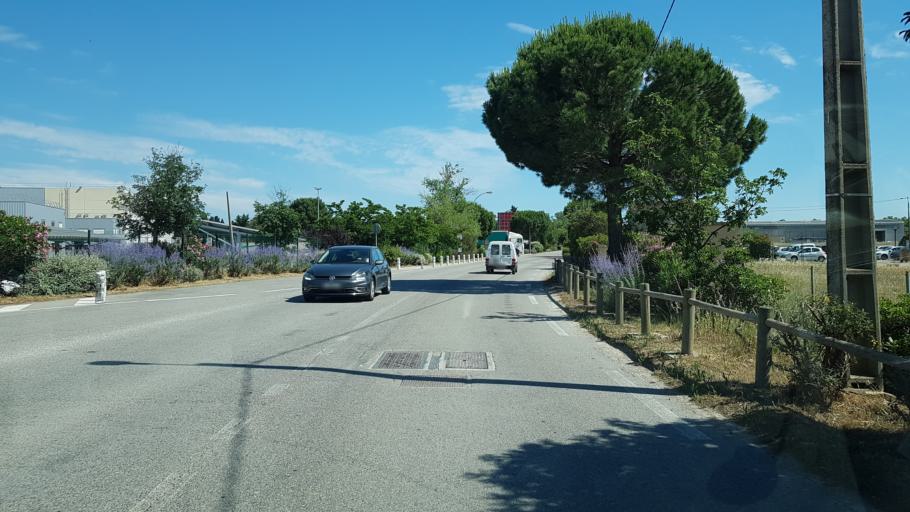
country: FR
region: Provence-Alpes-Cote d'Azur
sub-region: Departement des Bouches-du-Rhone
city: Saint-Martin-de-Crau
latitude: 43.6210
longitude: 4.7926
